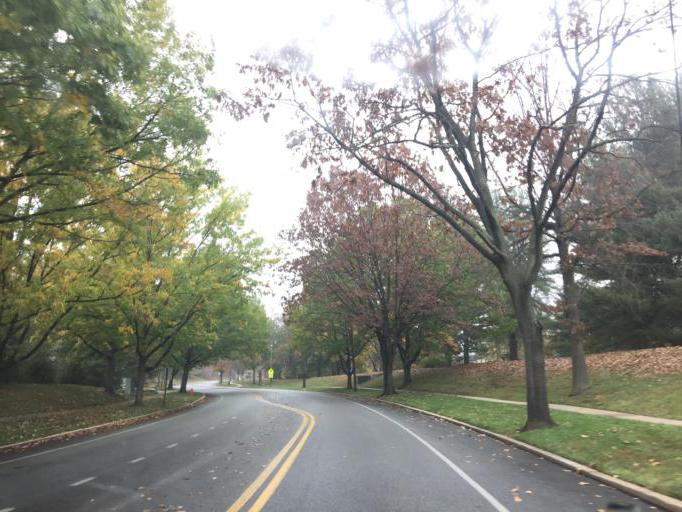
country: US
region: Maryland
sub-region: Howard County
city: Riverside
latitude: 39.1867
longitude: -76.8404
